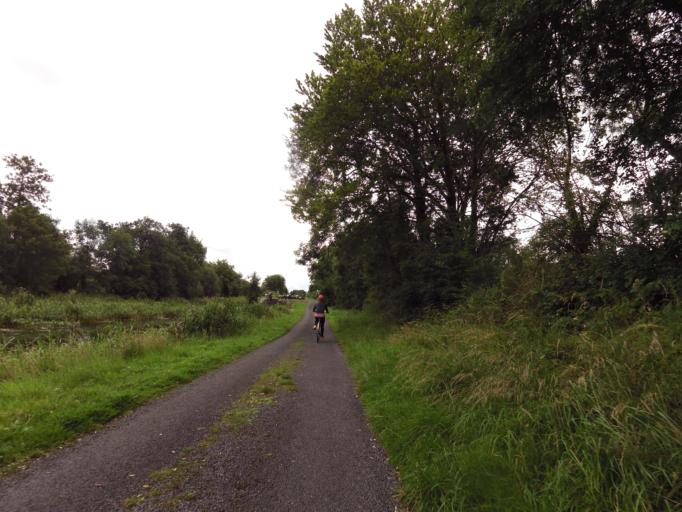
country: IE
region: Leinster
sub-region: An Iarmhi
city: An Muileann gCearr
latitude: 53.5379
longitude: -7.4739
